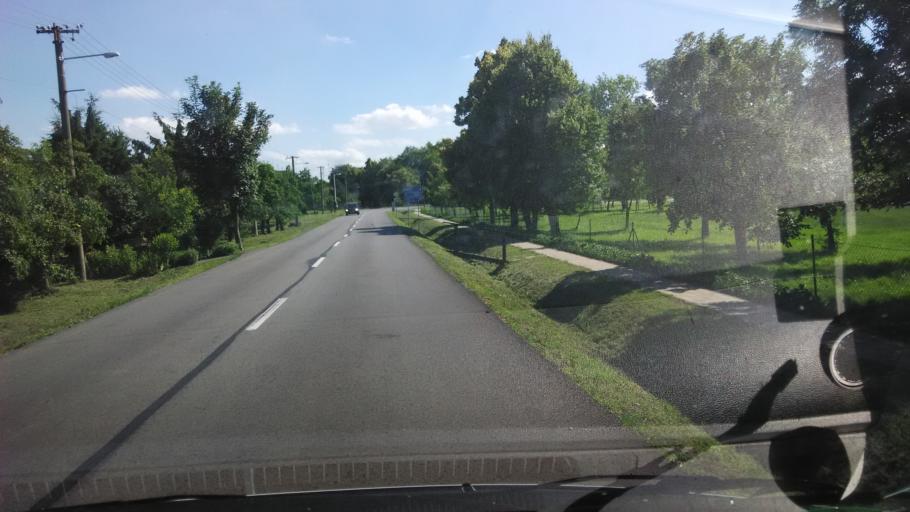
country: SK
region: Nitriansky
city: Tlmace
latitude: 48.1586
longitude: 18.4508
